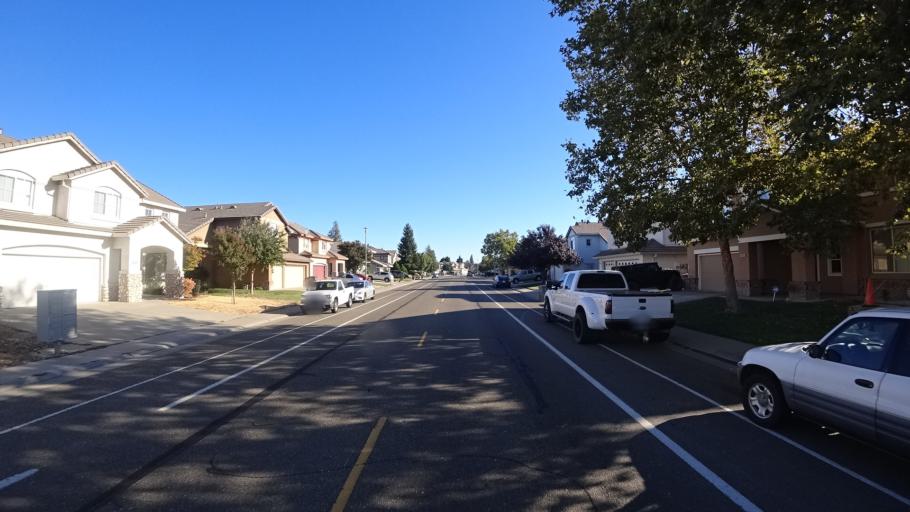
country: US
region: California
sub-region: Sacramento County
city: Elk Grove
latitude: 38.4459
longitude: -121.3854
